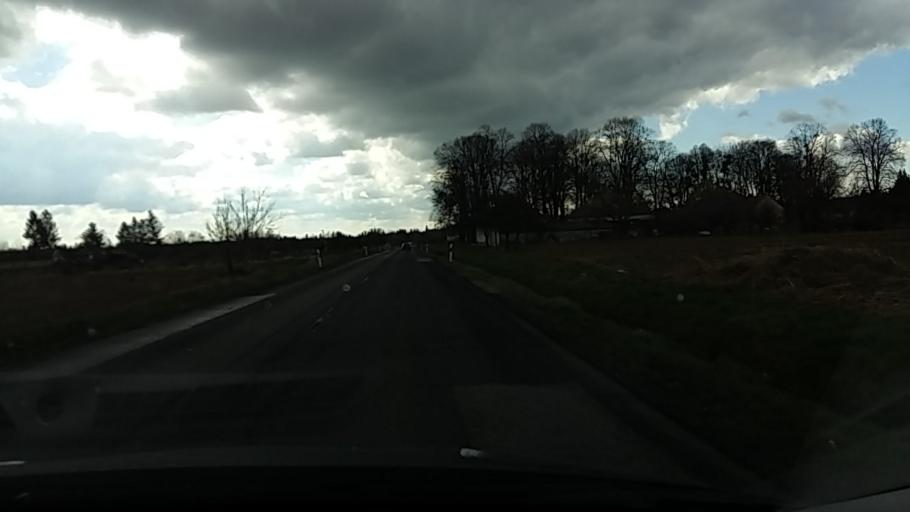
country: HU
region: Somogy
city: Bohonye
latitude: 46.4216
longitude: 17.3814
